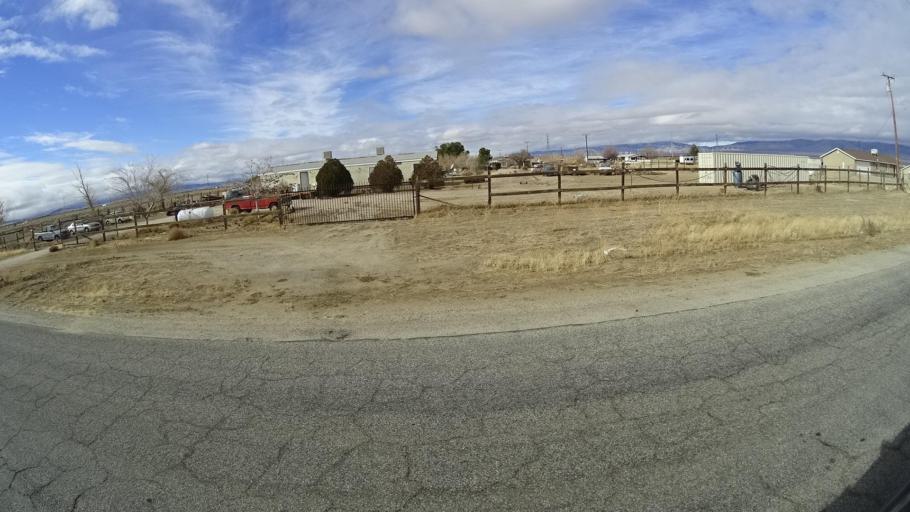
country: US
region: California
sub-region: Kern County
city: Rosamond
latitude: 34.8567
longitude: -118.3089
